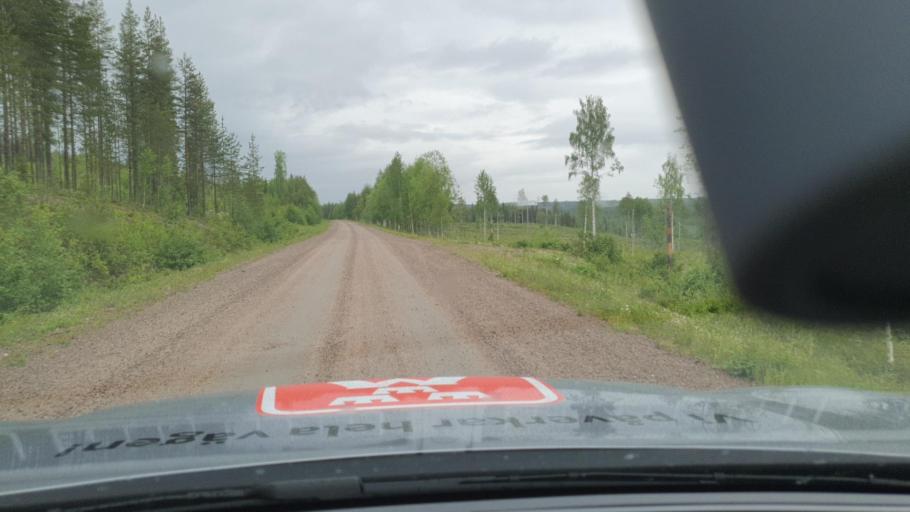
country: SE
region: Norrbotten
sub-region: Overkalix Kommun
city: OEverkalix
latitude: 66.5966
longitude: 22.7487
